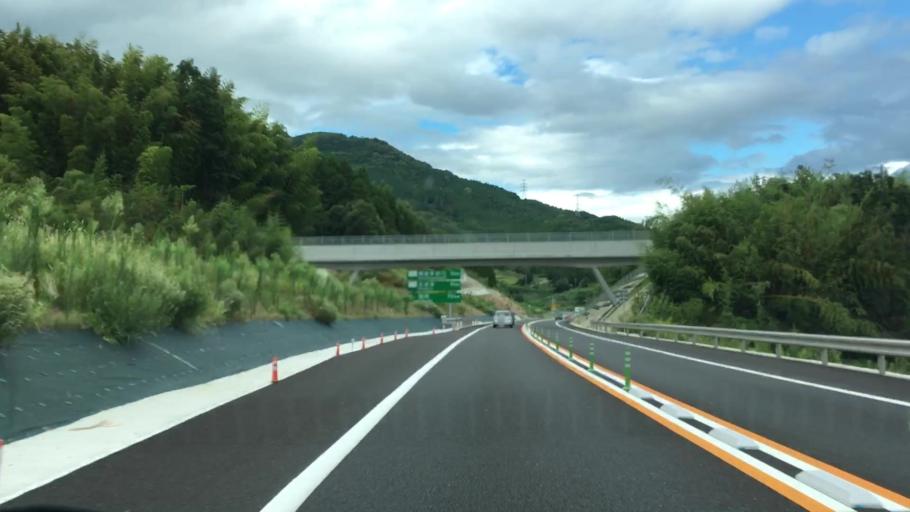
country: JP
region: Saga Prefecture
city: Imaricho-ko
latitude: 33.3083
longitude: 129.9164
